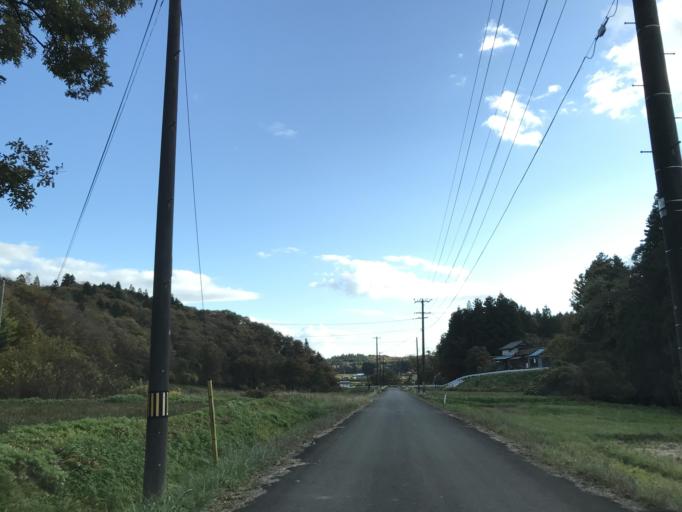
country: JP
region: Iwate
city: Ichinoseki
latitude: 38.8663
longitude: 141.1380
